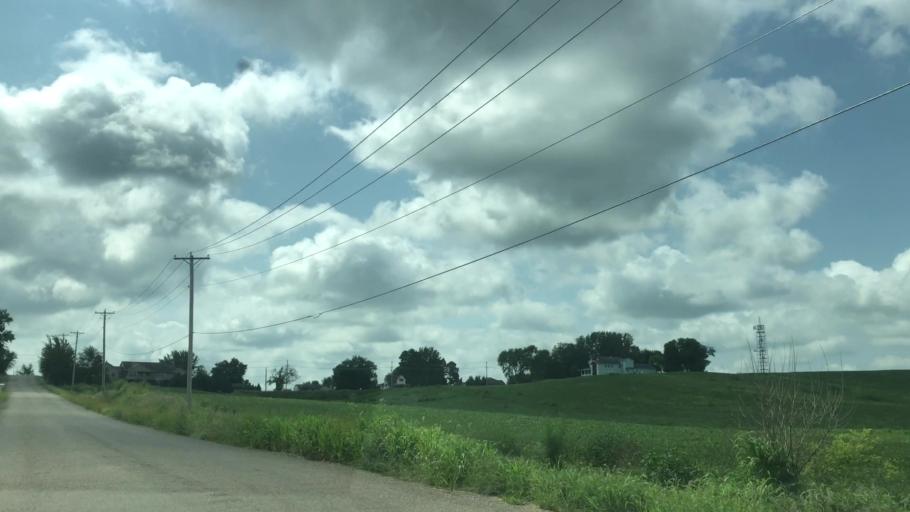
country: US
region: Iowa
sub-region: Marshall County
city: Marshalltown
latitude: 42.0524
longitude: -92.9565
